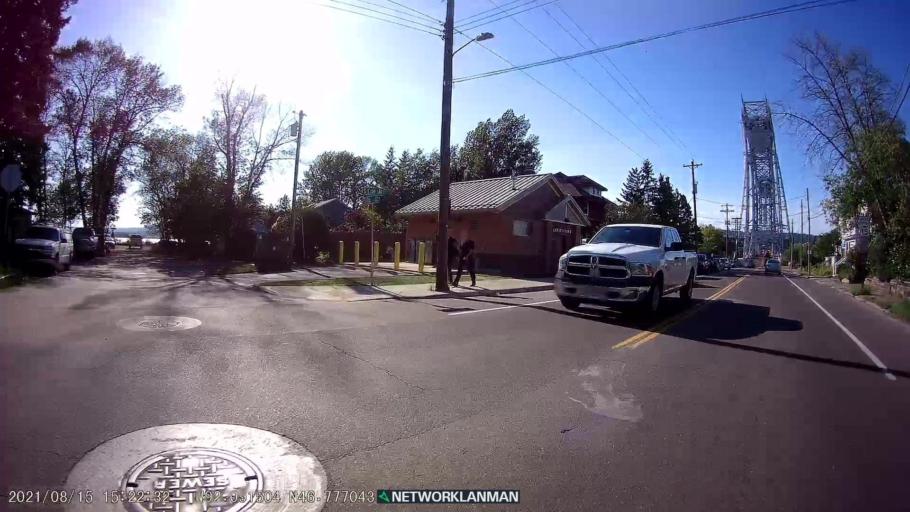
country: US
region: Minnesota
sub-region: Saint Louis County
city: Duluth
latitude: 46.7771
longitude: -92.0916
